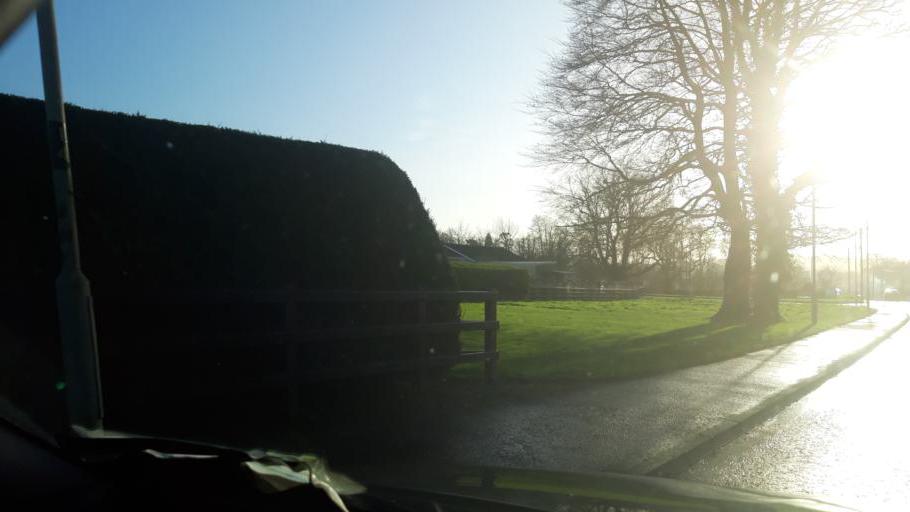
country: GB
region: Northern Ireland
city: Garvagh
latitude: 54.9897
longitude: -6.6849
